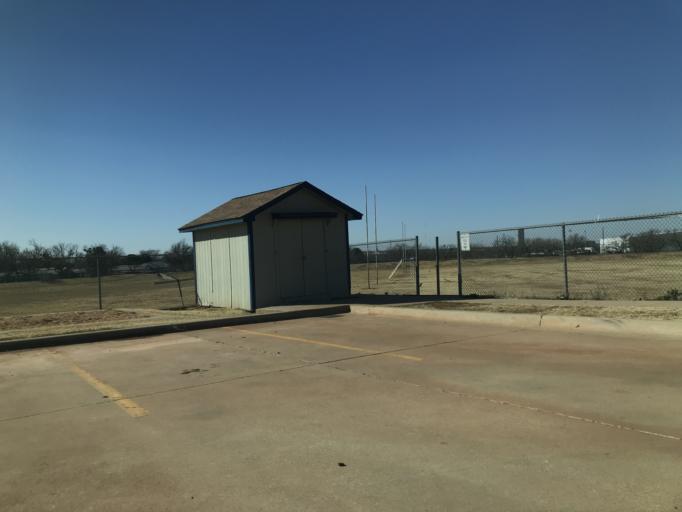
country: US
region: Texas
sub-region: Taylor County
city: Abilene
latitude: 32.4412
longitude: -99.7081
